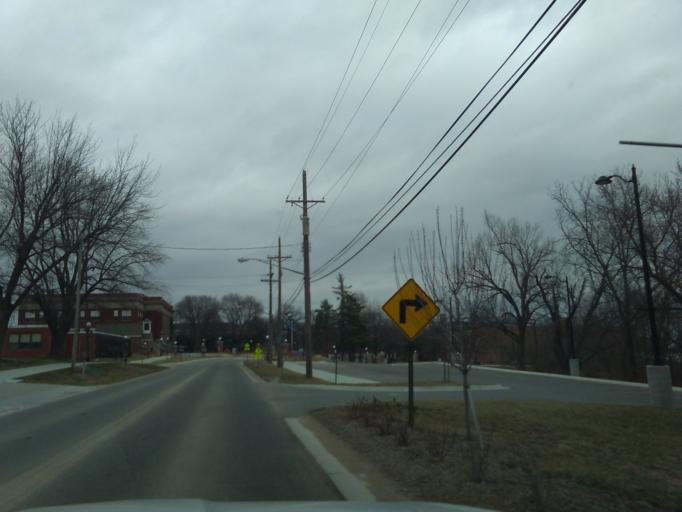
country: US
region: Nebraska
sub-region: Nemaha County
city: Auburn
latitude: 40.4726
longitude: -95.7337
